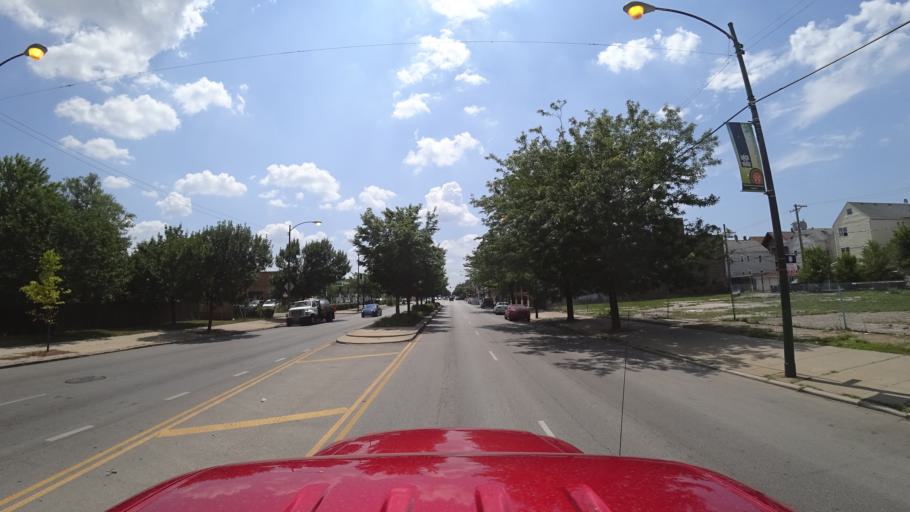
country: US
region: Illinois
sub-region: Cook County
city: Chicago
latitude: 41.8137
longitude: -87.6652
